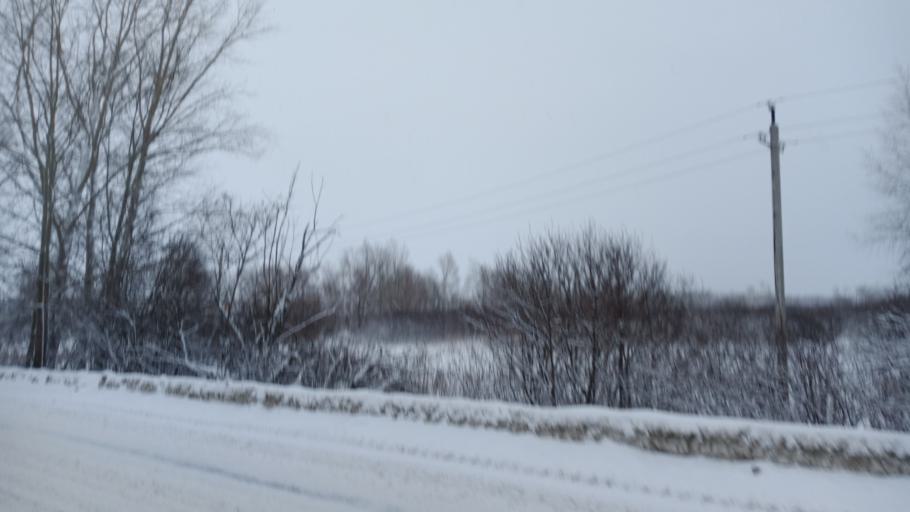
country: RU
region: Altai Krai
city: Zaton
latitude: 53.3125
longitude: 83.8310
